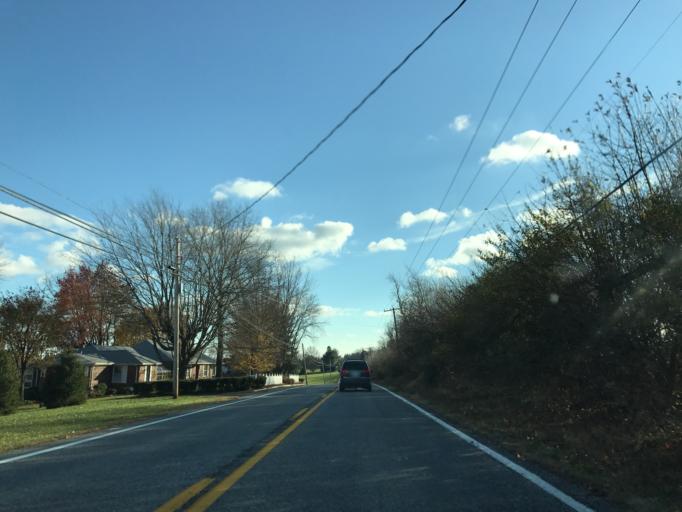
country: US
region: Maryland
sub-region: Harford County
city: Jarrettsville
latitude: 39.5666
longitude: -76.4989
